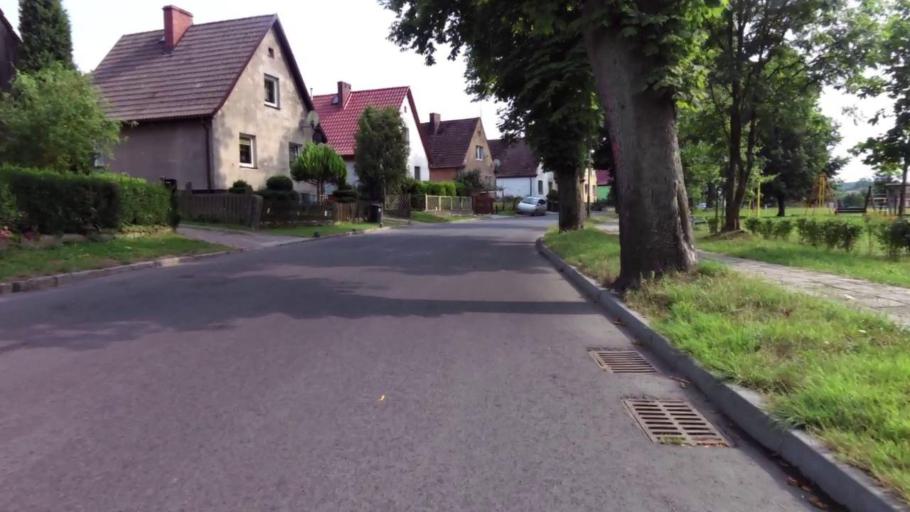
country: PL
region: West Pomeranian Voivodeship
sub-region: Powiat drawski
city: Zlocieniec
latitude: 53.5406
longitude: 16.0034
